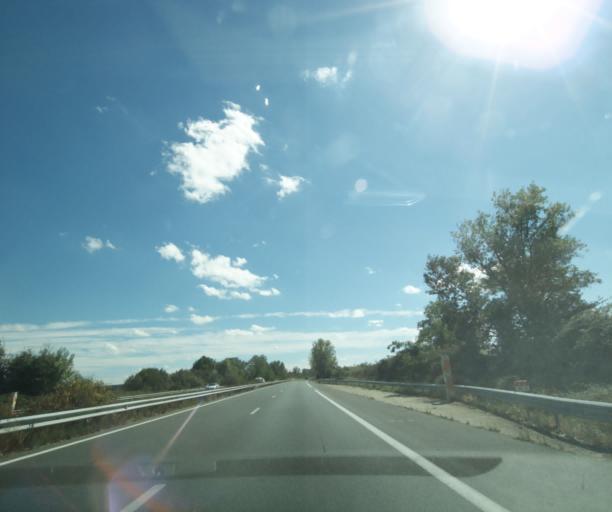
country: FR
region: Aquitaine
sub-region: Departement du Lot-et-Garonne
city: Tonneins
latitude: 44.3624
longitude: 0.2453
